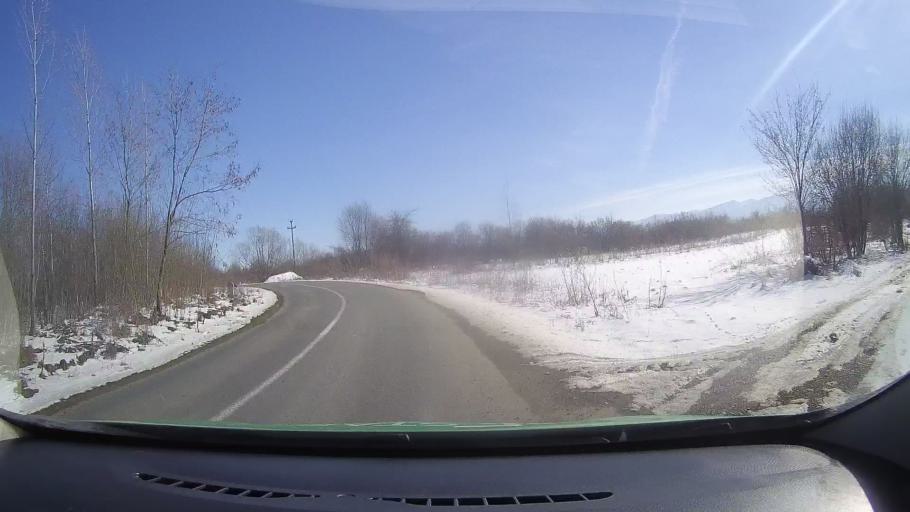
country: RO
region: Brasov
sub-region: Comuna Harseni
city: Harseni
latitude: 45.7338
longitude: 25.0106
